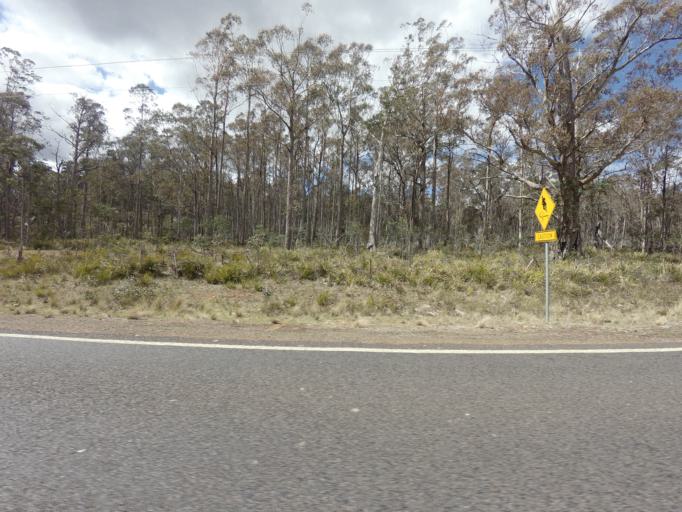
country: AU
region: Tasmania
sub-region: Northern Midlands
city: Evandale
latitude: -41.9999
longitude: 147.7198
